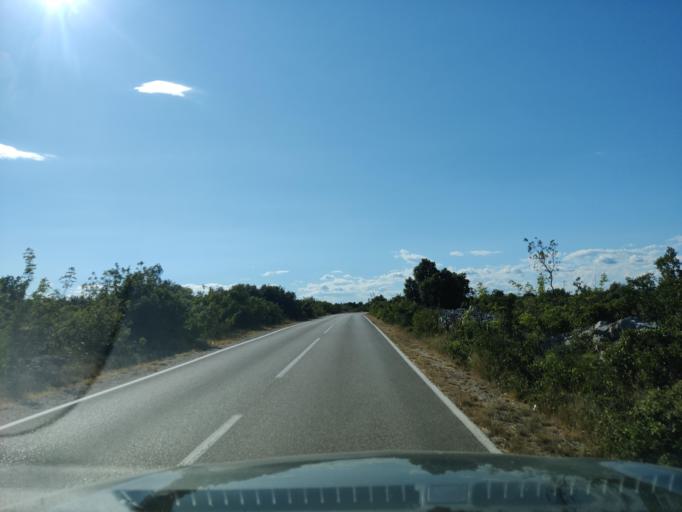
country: HR
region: Sibensko-Kniniska
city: Zaton
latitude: 43.7446
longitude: 15.8484
